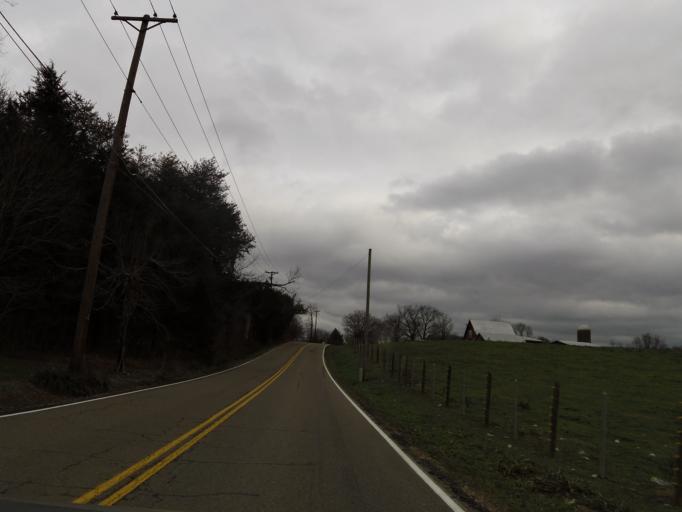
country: US
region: Tennessee
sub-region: Grainger County
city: Blaine
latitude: 36.1541
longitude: -83.7319
